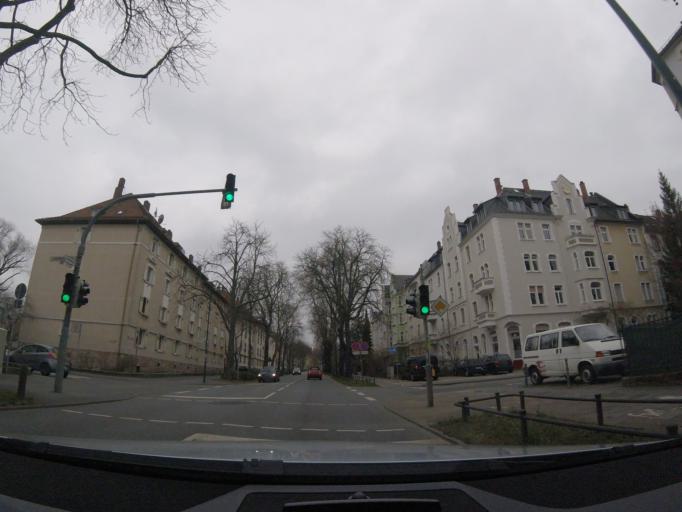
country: DE
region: Hesse
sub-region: Regierungsbezirk Darmstadt
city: Darmstadt
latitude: 49.8825
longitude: 8.6623
